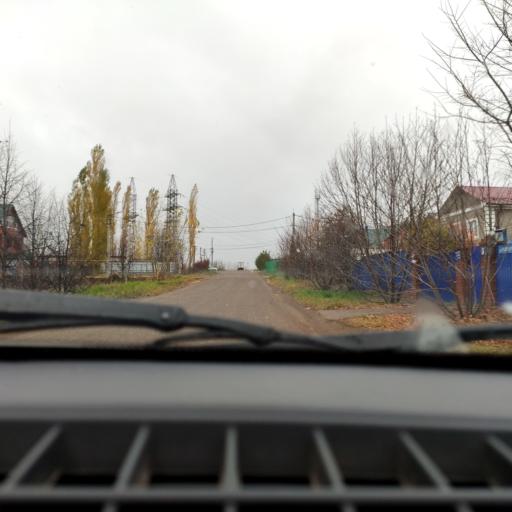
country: RU
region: Bashkortostan
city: Mikhaylovka
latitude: 54.8292
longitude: 55.9045
